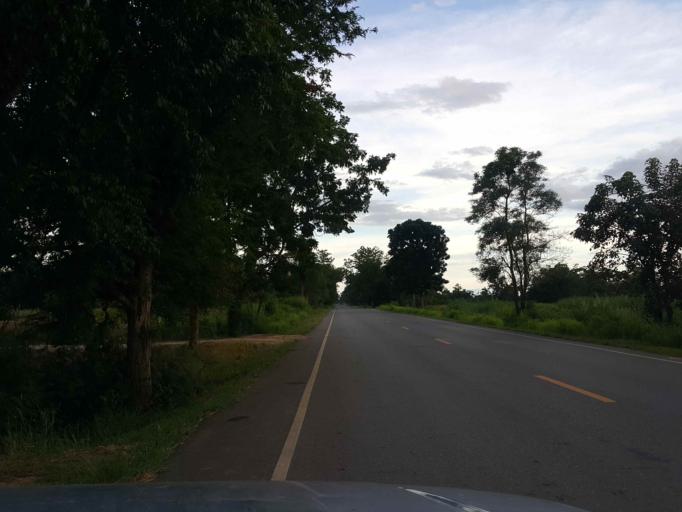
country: TH
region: Sukhothai
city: Sawankhalok
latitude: 17.3592
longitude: 99.7420
